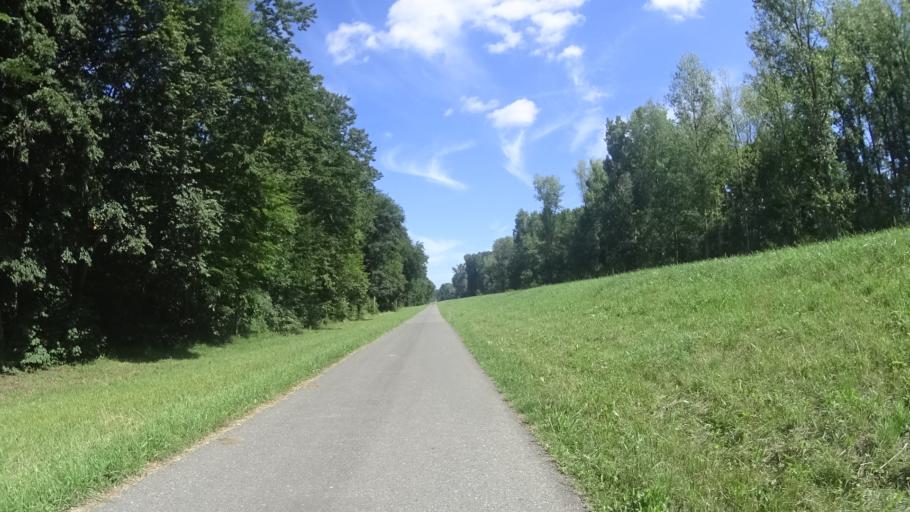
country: DE
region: Rheinland-Pfalz
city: Leimersheim
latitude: 49.1665
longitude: 8.3635
